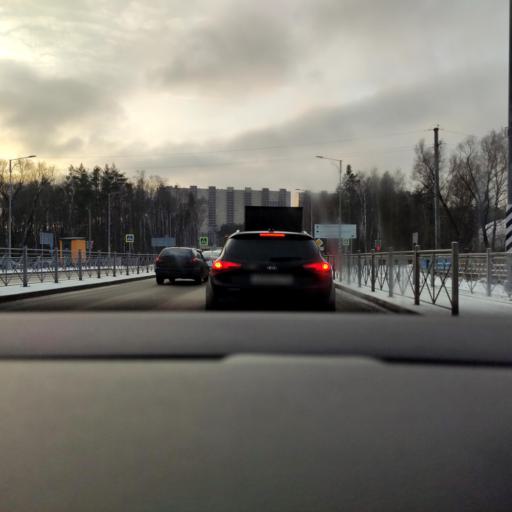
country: RU
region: Moskovskaya
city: Reutov
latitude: 55.7618
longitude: 37.8836
